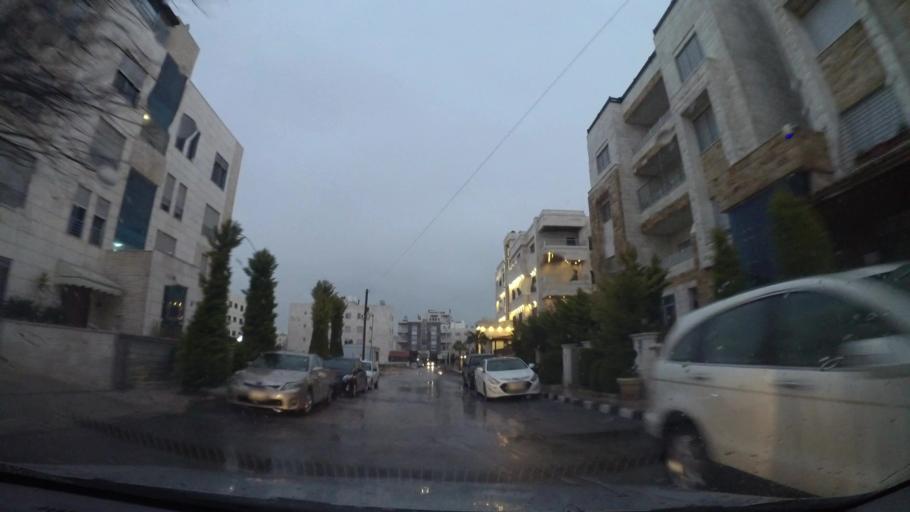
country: JO
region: Amman
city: Umm as Summaq
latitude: 31.9020
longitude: 35.8596
